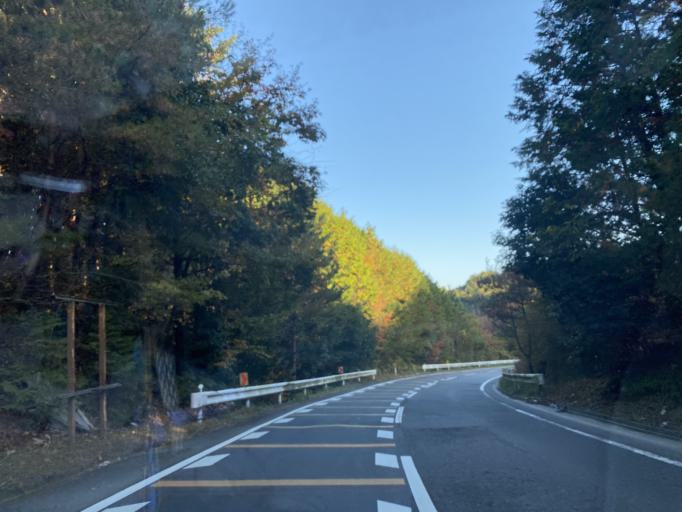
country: JP
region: Kyoto
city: Uji
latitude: 34.8946
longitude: 135.8876
